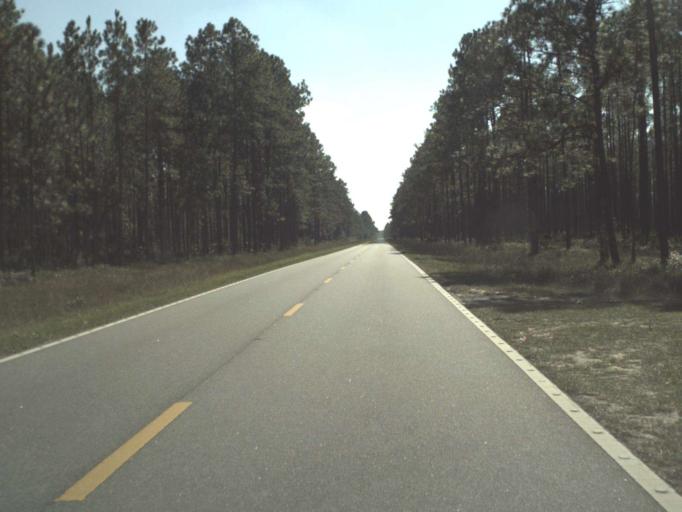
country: US
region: Florida
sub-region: Gulf County
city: Wewahitchka
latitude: 30.1166
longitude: -84.9879
